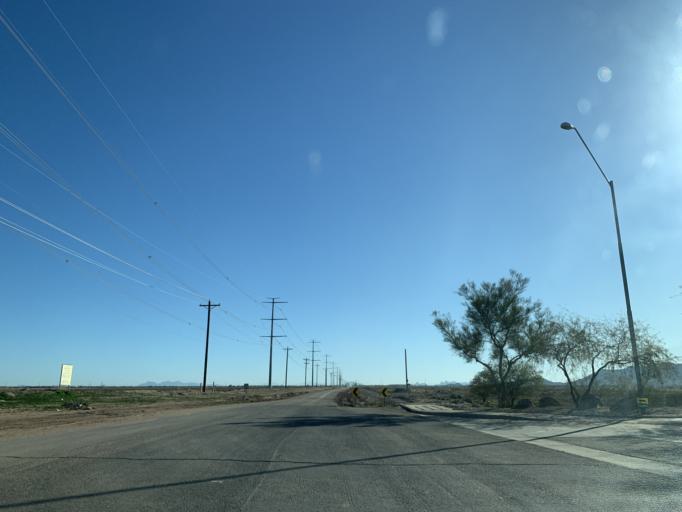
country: US
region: Arizona
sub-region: Pinal County
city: Casa Grande
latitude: 32.8651
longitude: -111.6709
